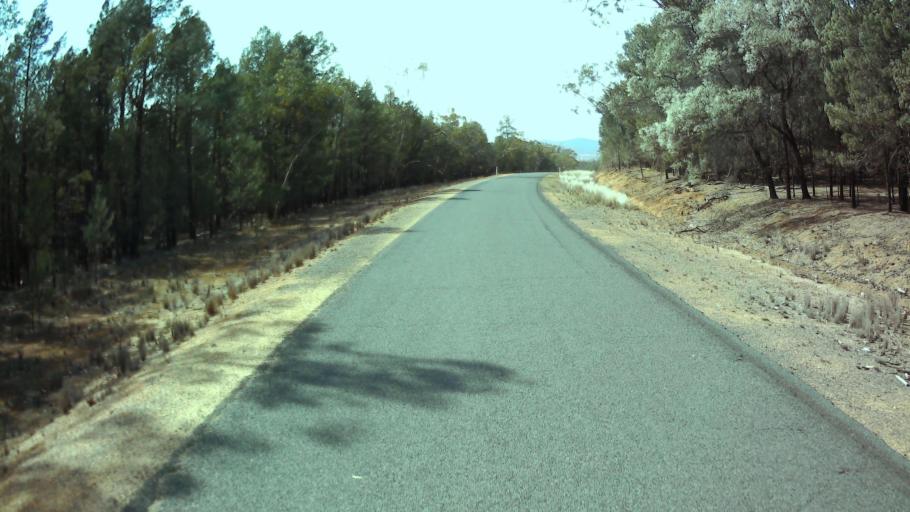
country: AU
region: New South Wales
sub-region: Weddin
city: Grenfell
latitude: -33.7441
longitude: 148.0533
